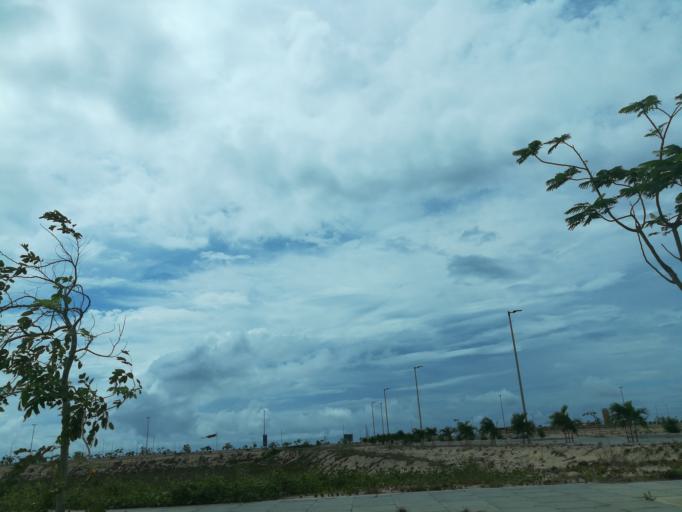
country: NG
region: Lagos
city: Lagos
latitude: 6.4089
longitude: 3.4124
